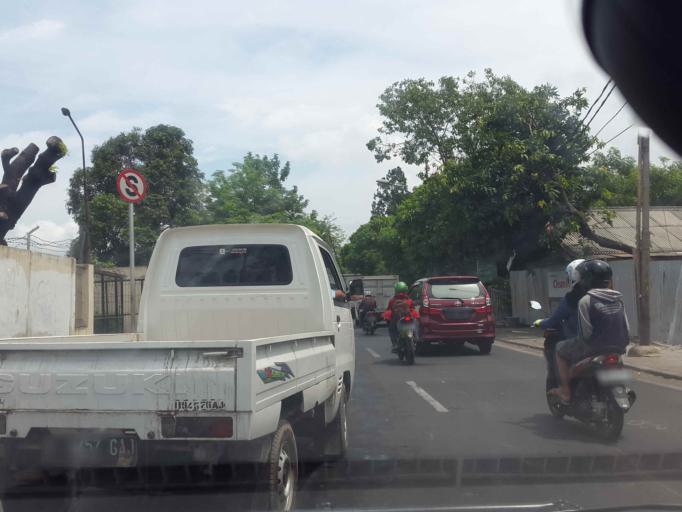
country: ID
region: Banten
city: Tangerang
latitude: -6.1675
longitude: 106.6307
